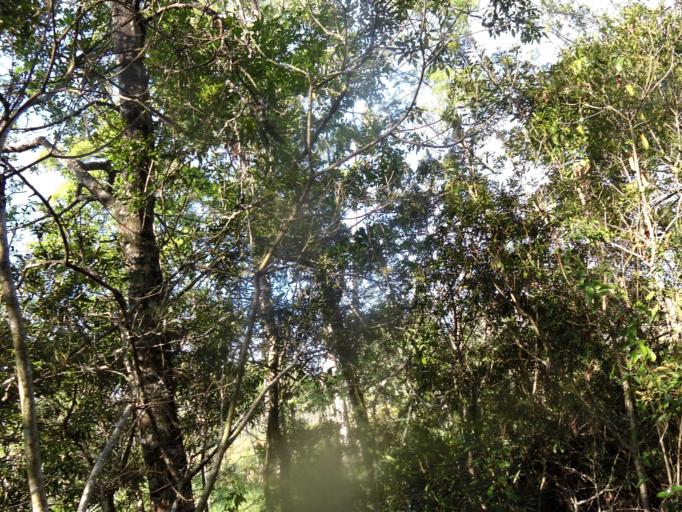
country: US
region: Florida
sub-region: Clay County
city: Bellair-Meadowbrook Terrace
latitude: 30.2461
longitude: -81.7046
